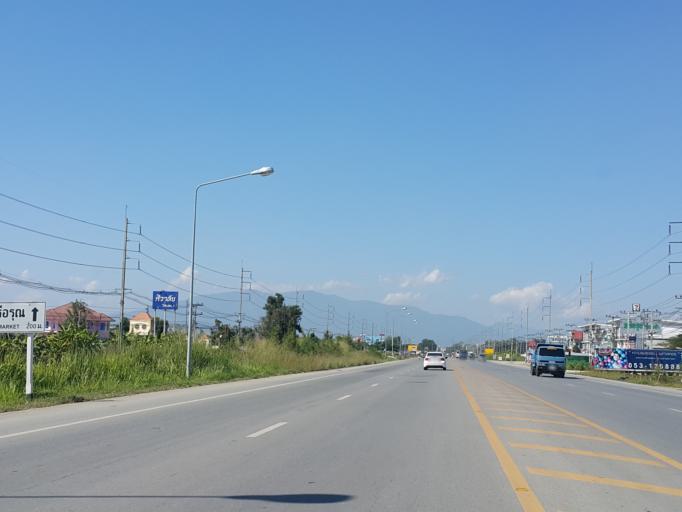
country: TH
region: Chiang Mai
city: San Kamphaeng
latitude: 18.7379
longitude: 99.0850
